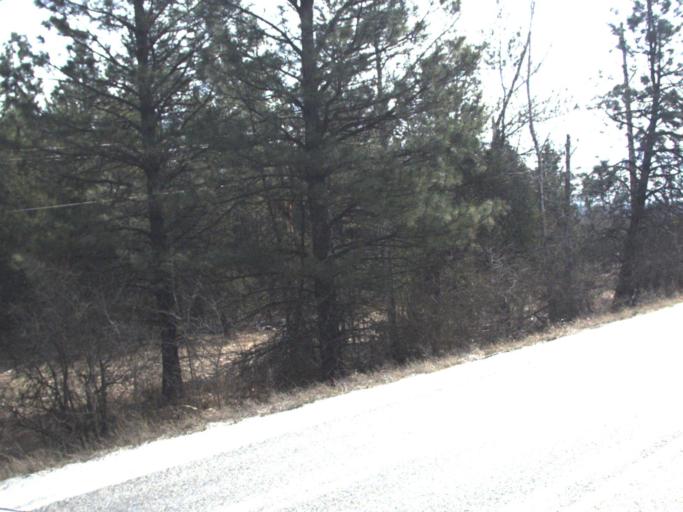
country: US
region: Washington
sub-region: Pend Oreille County
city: Newport
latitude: 48.3884
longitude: -117.3126
